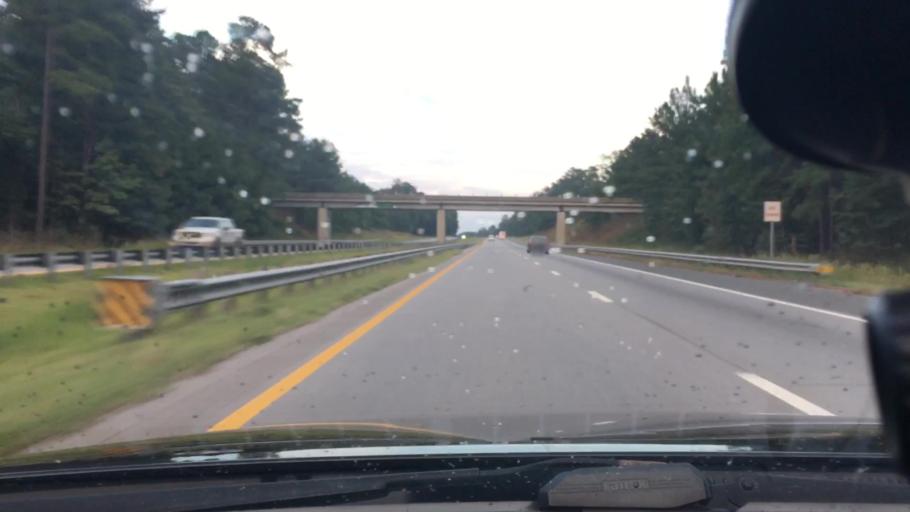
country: US
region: North Carolina
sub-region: Wake County
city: Holly Springs
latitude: 35.6489
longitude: -78.9701
